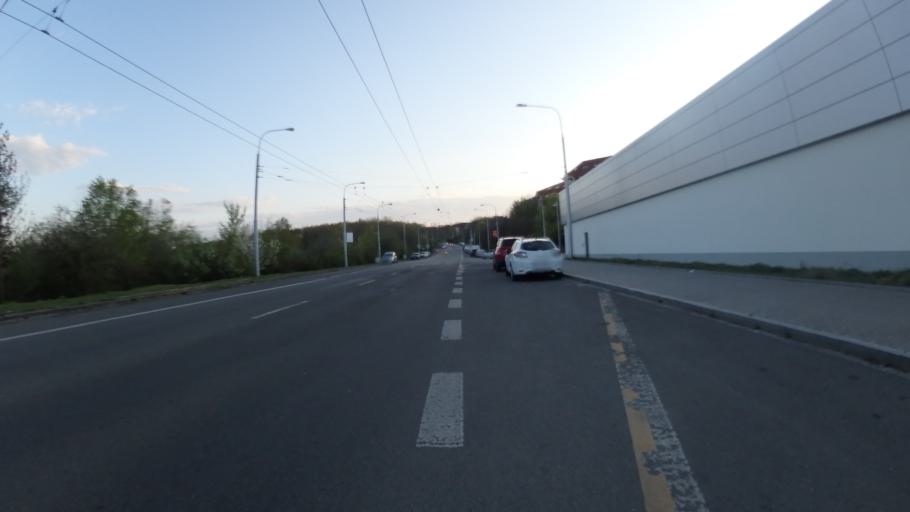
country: CZ
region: South Moravian
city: Troubsko
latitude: 49.1957
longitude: 16.5331
